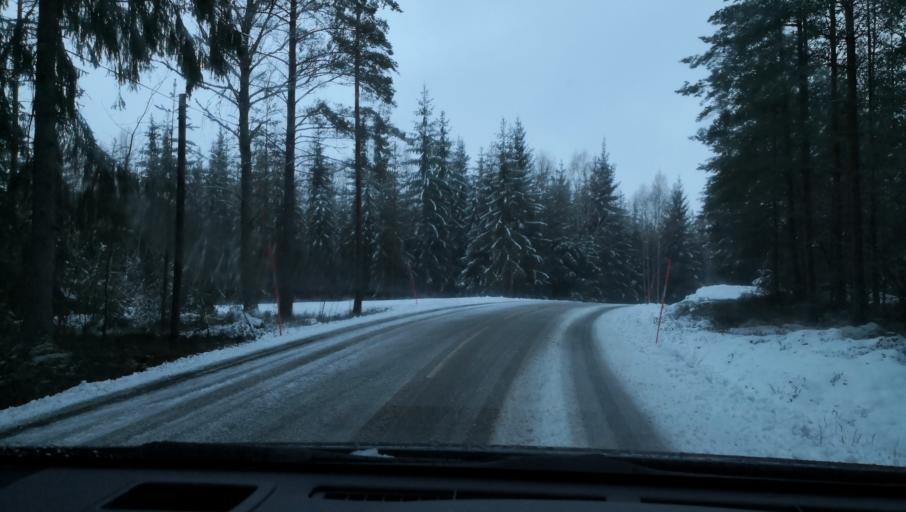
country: SE
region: Vaestmanland
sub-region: Kopings Kommun
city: Kolsva
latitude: 59.5689
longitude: 15.7921
